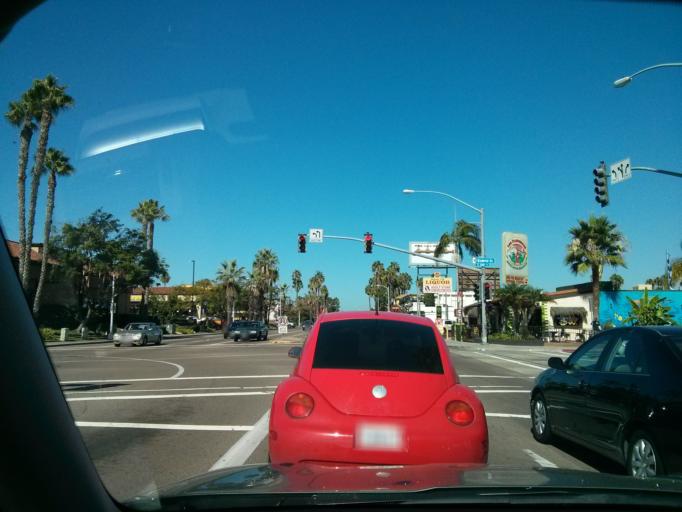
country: US
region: California
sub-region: San Diego County
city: San Diego
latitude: 32.7520
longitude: -117.2149
